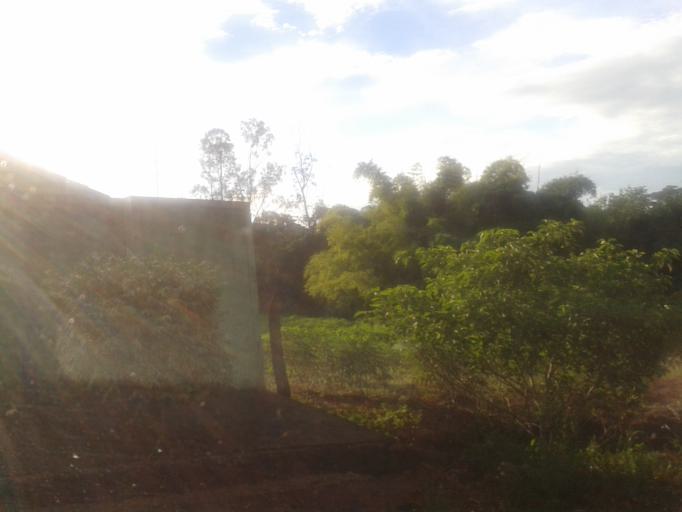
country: BR
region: Minas Gerais
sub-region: Capinopolis
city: Capinopolis
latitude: -18.6768
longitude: -49.5662
